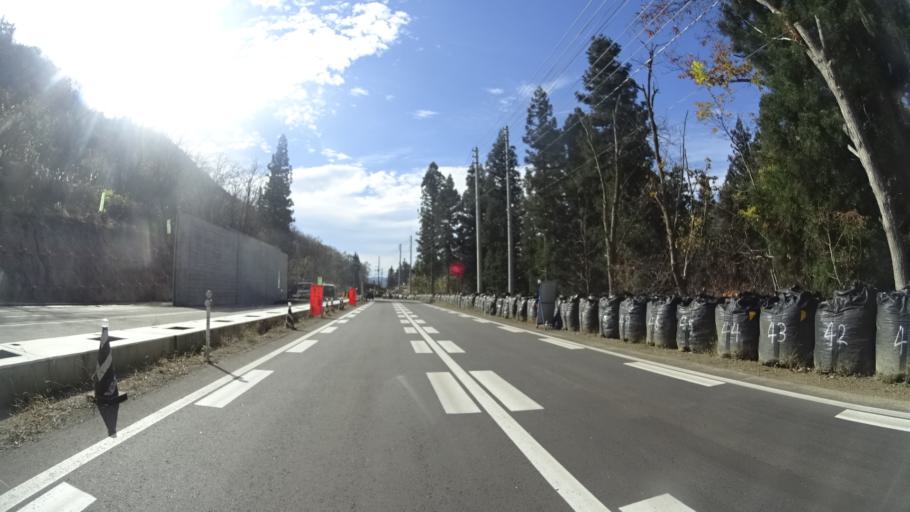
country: JP
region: Niigata
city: Ojiya
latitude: 37.2716
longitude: 138.9870
